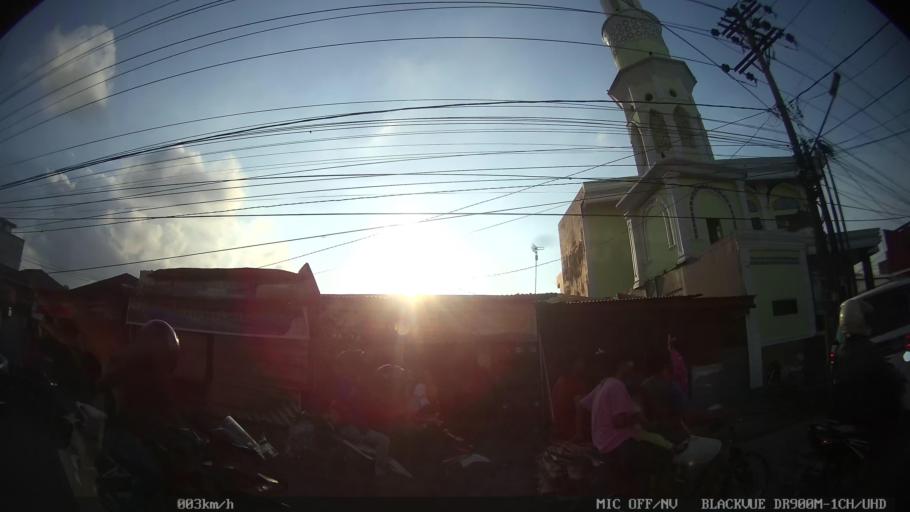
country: ID
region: North Sumatra
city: Medan
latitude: 3.6041
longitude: 98.6651
